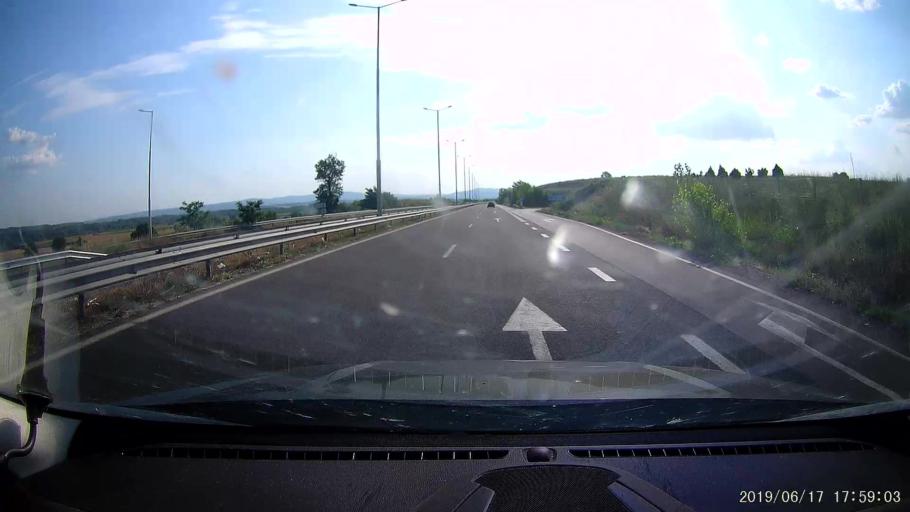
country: BG
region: Khaskovo
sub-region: Obshtina Svilengrad
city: Svilengrad
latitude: 41.7253
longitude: 26.3080
